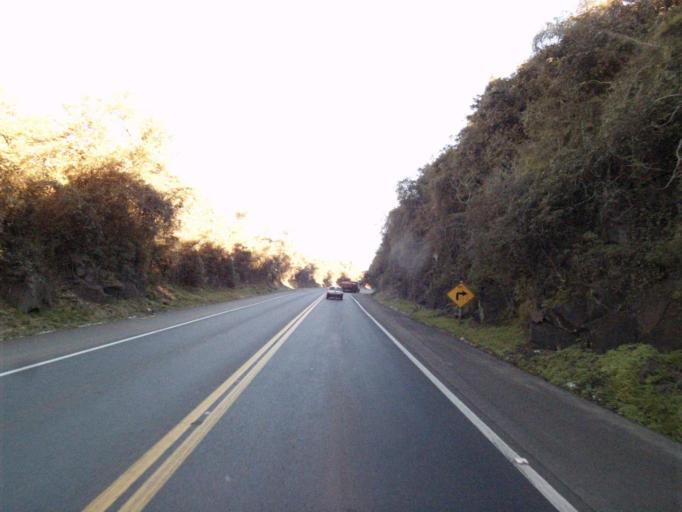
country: BR
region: Santa Catarina
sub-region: Chapeco
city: Chapeco
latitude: -26.9724
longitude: -52.5829
